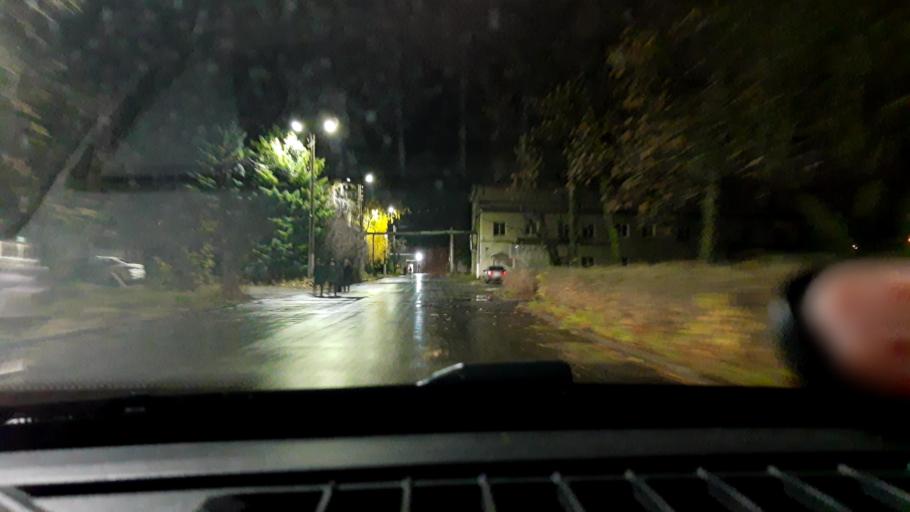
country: RU
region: Nizjnij Novgorod
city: Burevestnik
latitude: 56.2375
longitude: 43.8754
